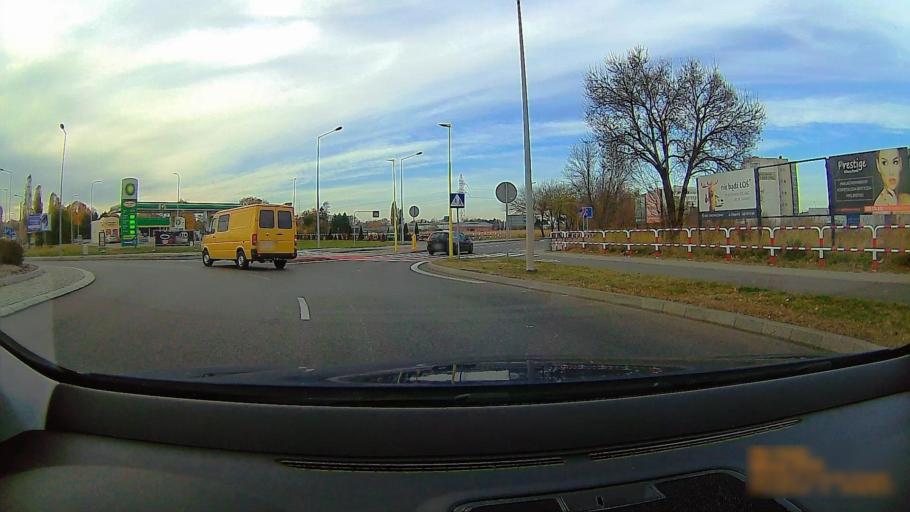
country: PL
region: Greater Poland Voivodeship
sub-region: Kalisz
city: Kalisz
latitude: 51.7707
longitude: 18.0707
